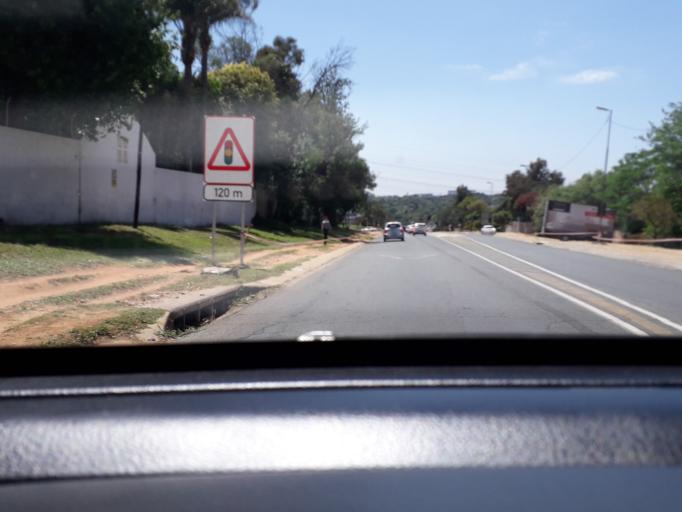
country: ZA
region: Gauteng
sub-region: City of Johannesburg Metropolitan Municipality
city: Modderfontein
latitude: -26.0909
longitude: 28.0617
